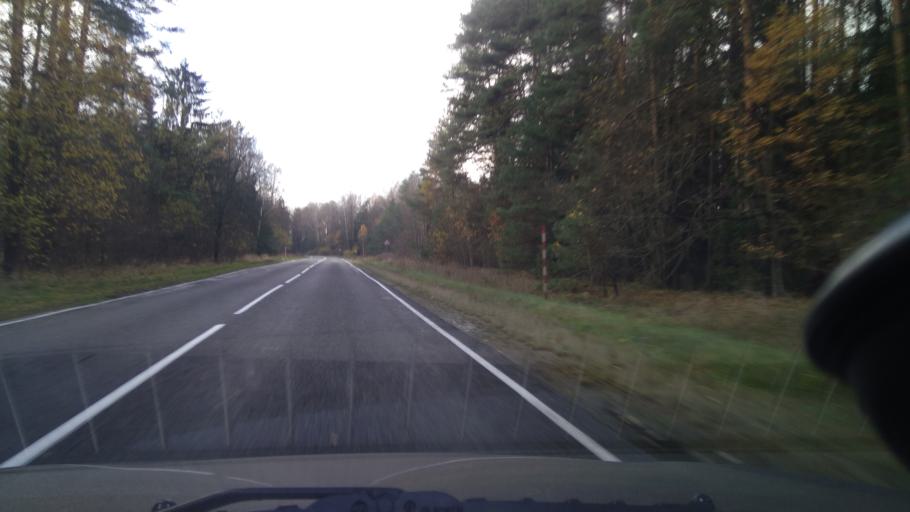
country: BY
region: Minsk
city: Slutsk
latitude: 53.2321
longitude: 27.6416
